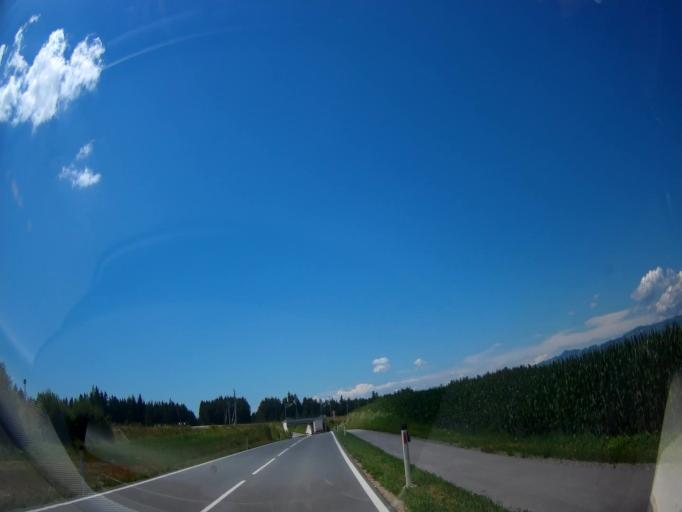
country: AT
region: Carinthia
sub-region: Politischer Bezirk Volkermarkt
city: Eberndorf
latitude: 46.6109
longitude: 14.6759
